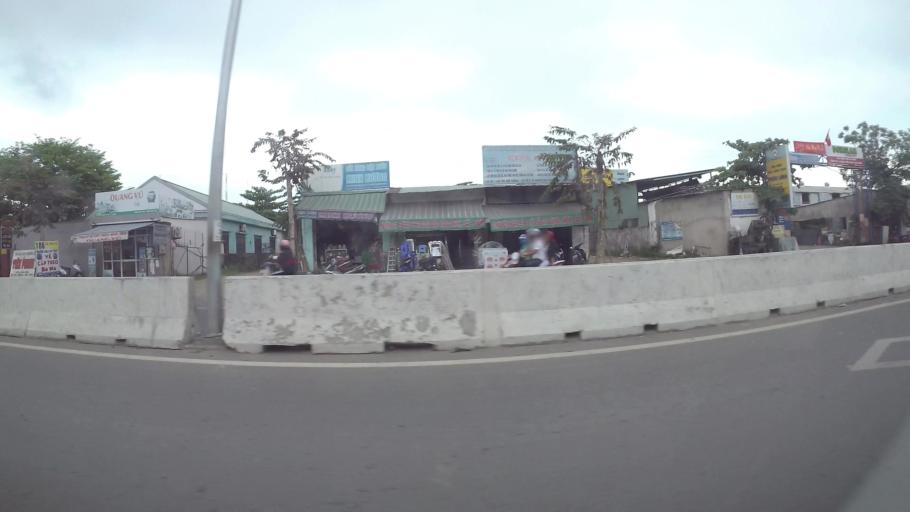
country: VN
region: Da Nang
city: Lien Chieu
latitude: 16.0541
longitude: 108.1587
